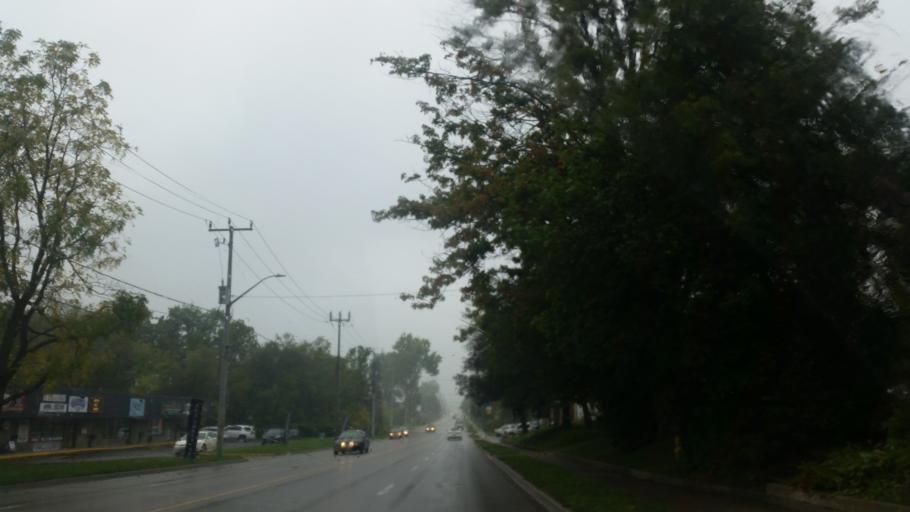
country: CA
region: Ontario
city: Stratford
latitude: 43.3613
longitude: -80.9914
